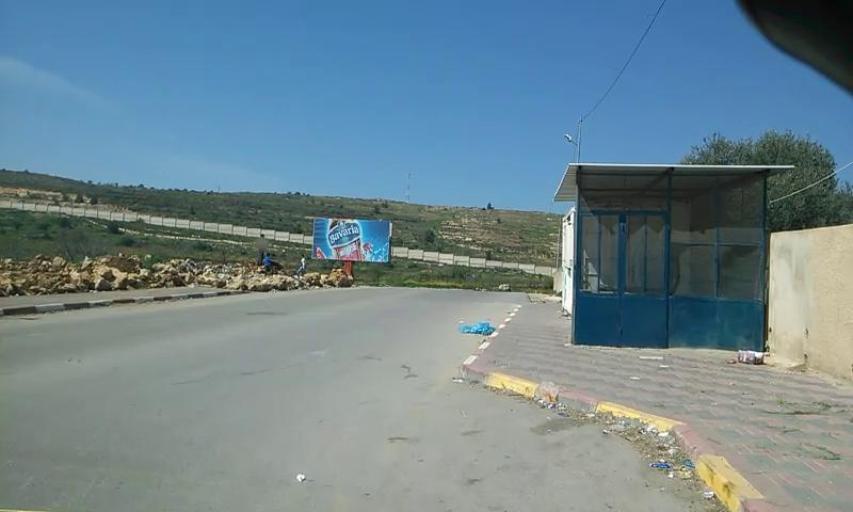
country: PS
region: West Bank
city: Al Khadir
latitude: 31.7029
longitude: 35.1606
